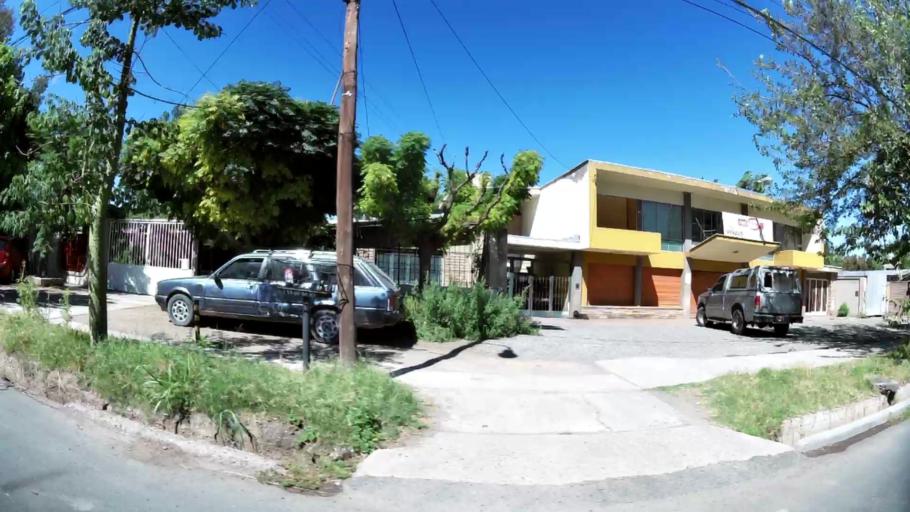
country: AR
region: Mendoza
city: Las Heras
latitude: -32.8283
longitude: -68.8393
